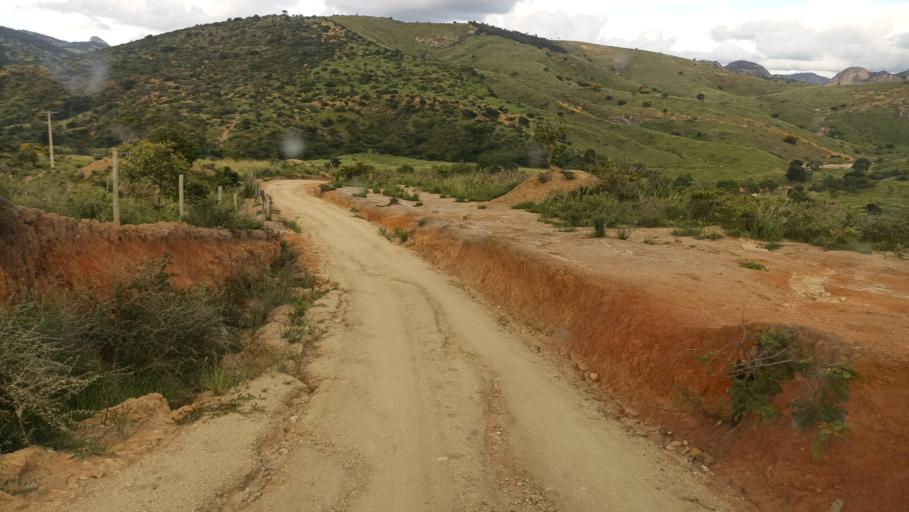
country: BR
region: Minas Gerais
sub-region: Almenara
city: Almenara
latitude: -16.5385
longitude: -40.4444
